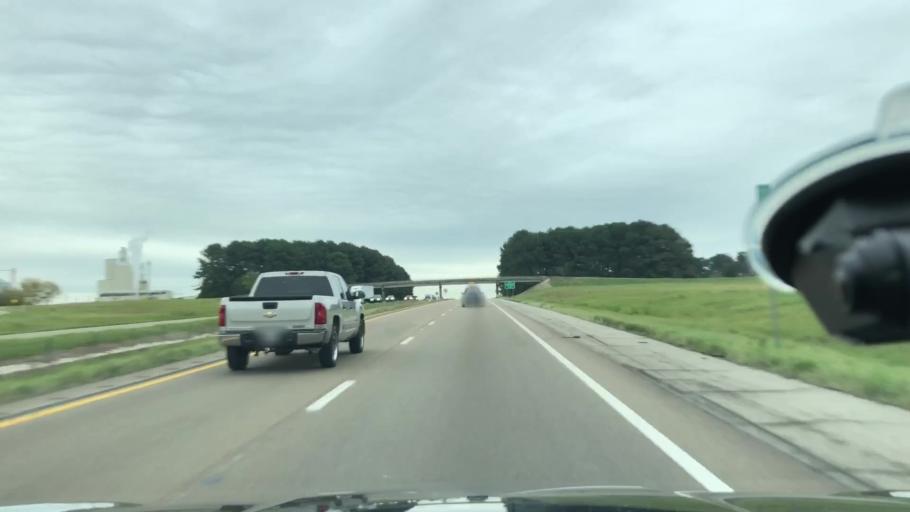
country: US
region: Texas
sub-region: Titus County
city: Mount Pleasant
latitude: 33.1593
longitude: -95.0765
